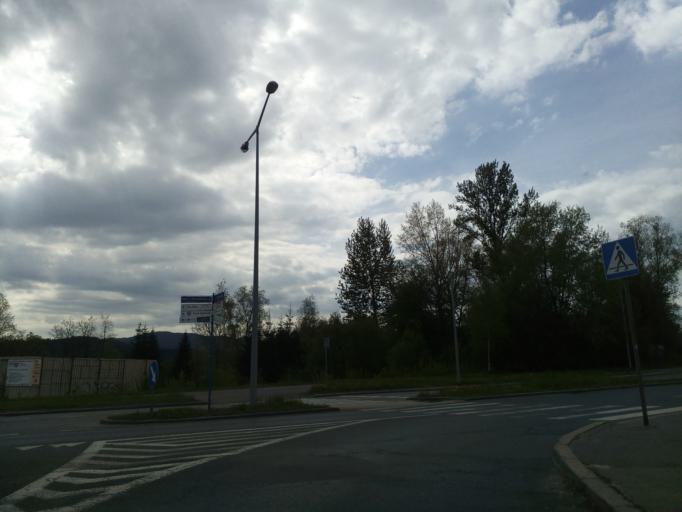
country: PL
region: Lesser Poland Voivodeship
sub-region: Powiat nowosadecki
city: Nawojowa
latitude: 49.5889
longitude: 20.7250
